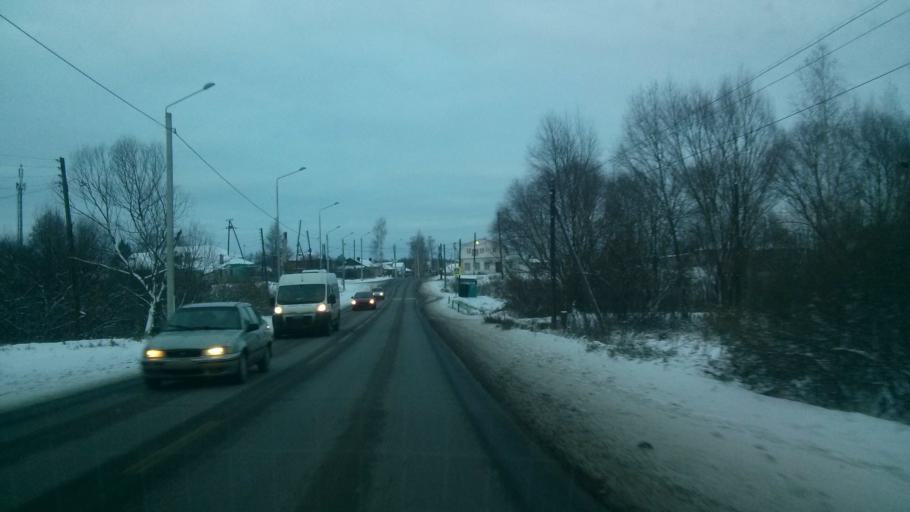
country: RU
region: Nizjnij Novgorod
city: Vorsma
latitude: 56.0360
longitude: 43.3681
